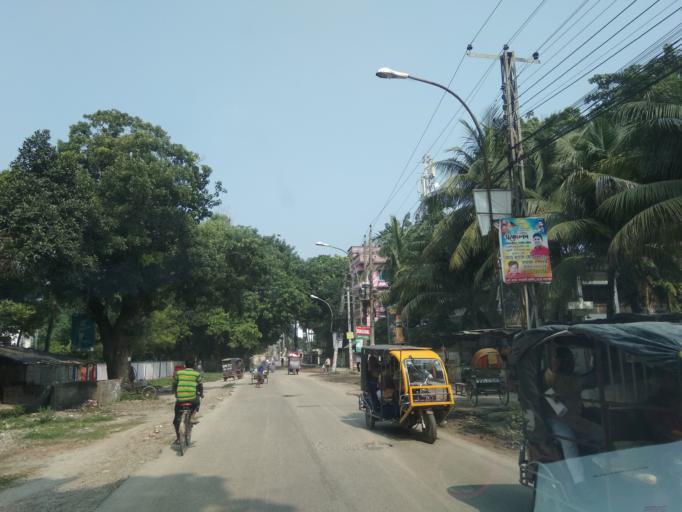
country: BD
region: Rangpur Division
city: Rangpur
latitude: 25.7579
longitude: 89.2365
